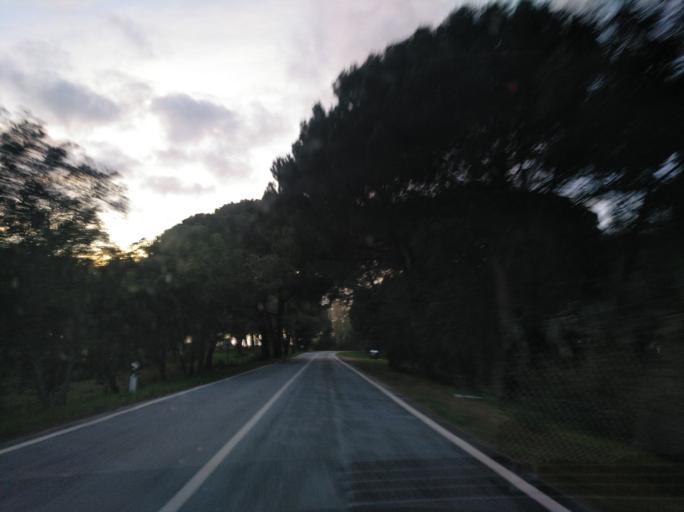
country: PT
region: Setubal
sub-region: Grandola
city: Grandola
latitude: 38.2007
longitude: -8.6203
